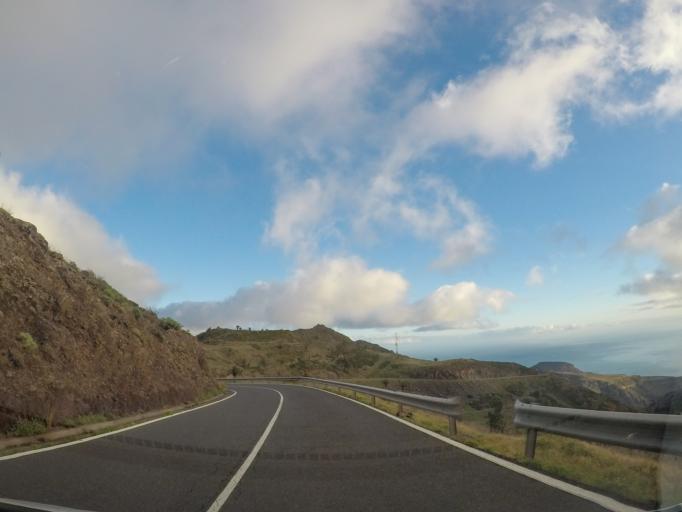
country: ES
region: Canary Islands
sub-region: Provincia de Santa Cruz de Tenerife
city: Alajero
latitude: 28.0856
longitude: -17.2467
